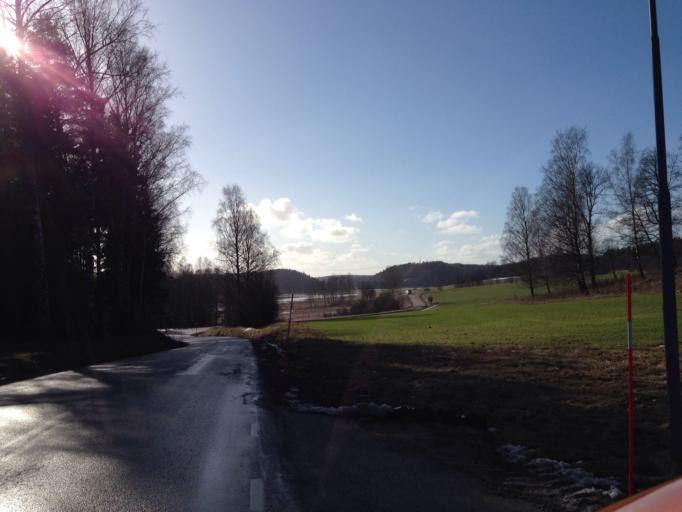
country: SE
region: Stockholm
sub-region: Botkyrka Kommun
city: Varsta
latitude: 59.1437
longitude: 17.7889
